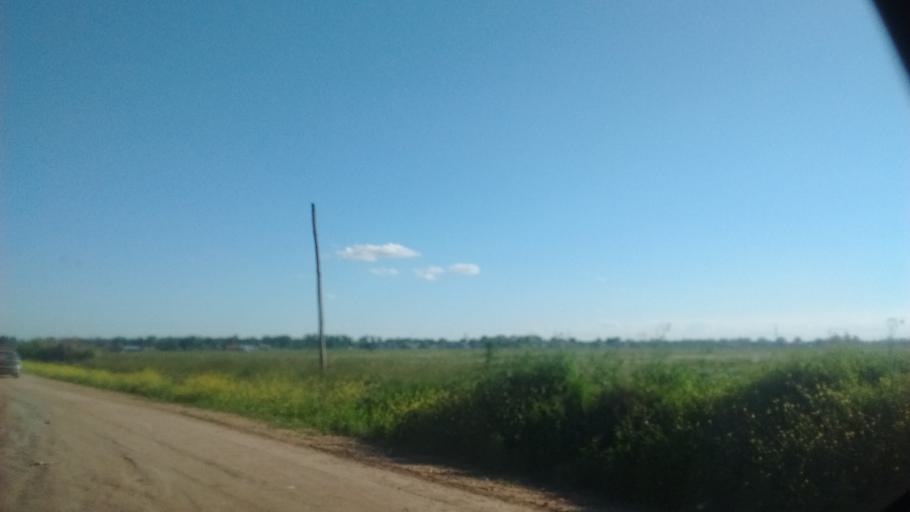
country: AR
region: Santa Fe
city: Funes
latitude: -32.8938
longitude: -60.8053
